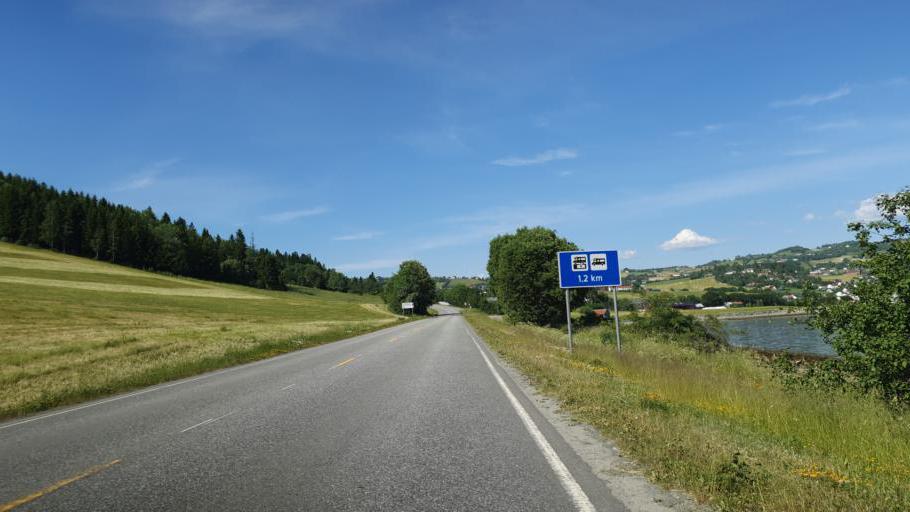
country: NO
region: Nord-Trondelag
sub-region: Leksvik
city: Leksvik
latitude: 63.6610
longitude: 10.6083
